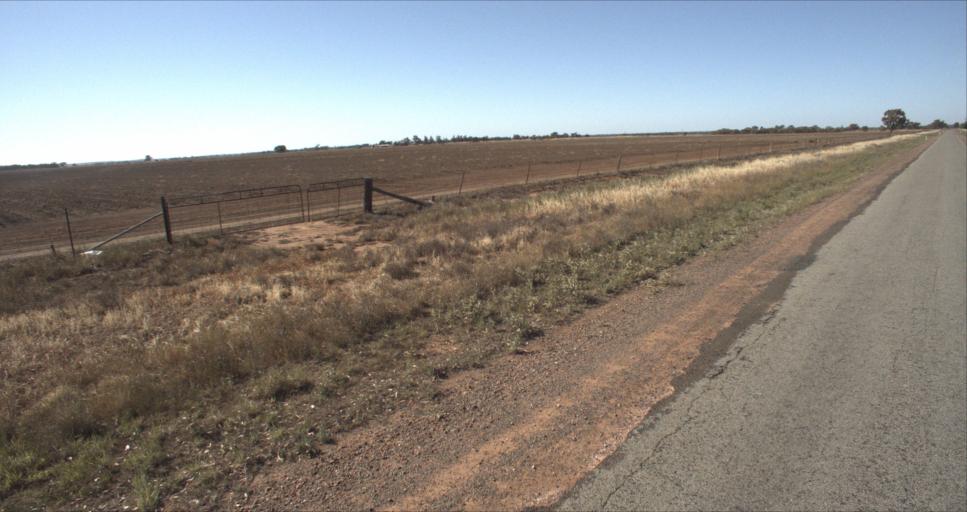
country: AU
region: New South Wales
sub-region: Leeton
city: Leeton
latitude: -34.5605
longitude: 146.3128
